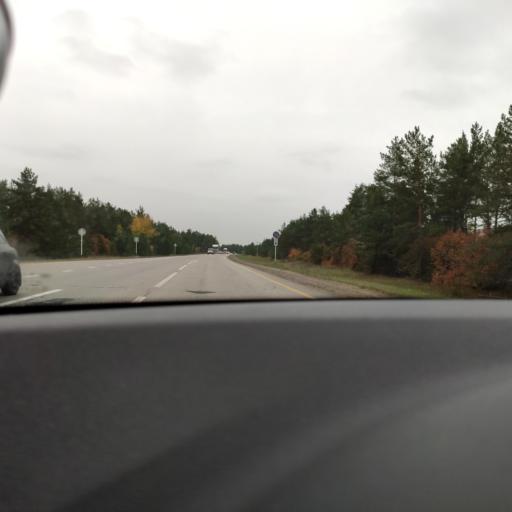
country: RU
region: Samara
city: Mirnyy
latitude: 53.5369
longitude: 50.3008
